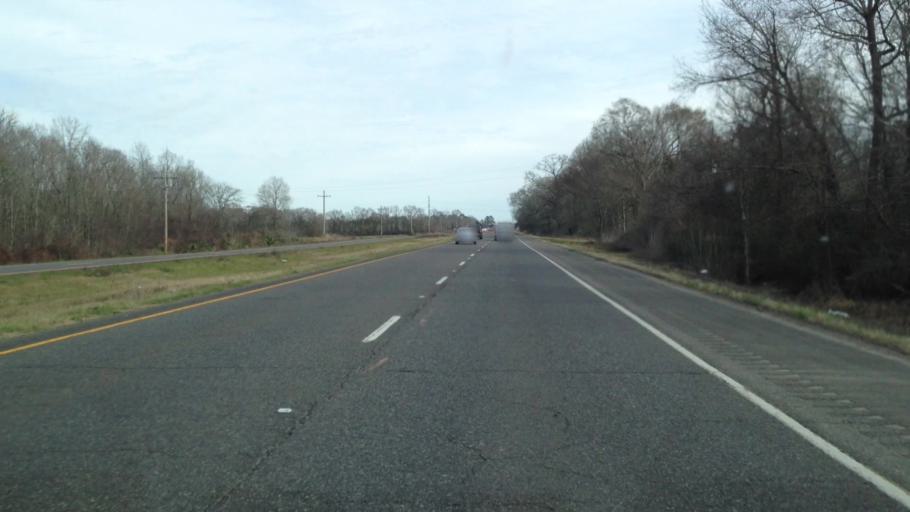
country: US
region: Louisiana
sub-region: Saint Landry Parish
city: Port Barre
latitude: 30.5476
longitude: -91.9833
